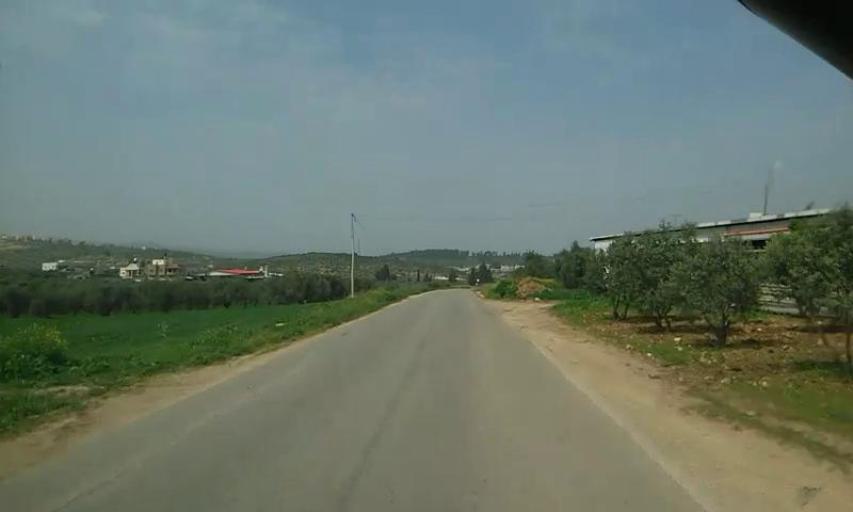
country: PS
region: West Bank
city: Zububah
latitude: 32.5322
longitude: 35.2170
